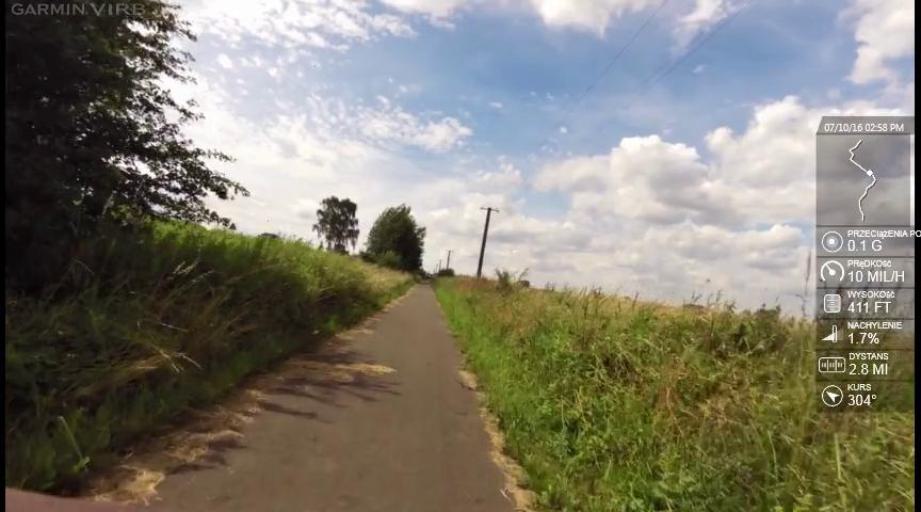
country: PL
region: West Pomeranian Voivodeship
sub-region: Powiat gryfinski
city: Banie
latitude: 53.1067
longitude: 14.6417
